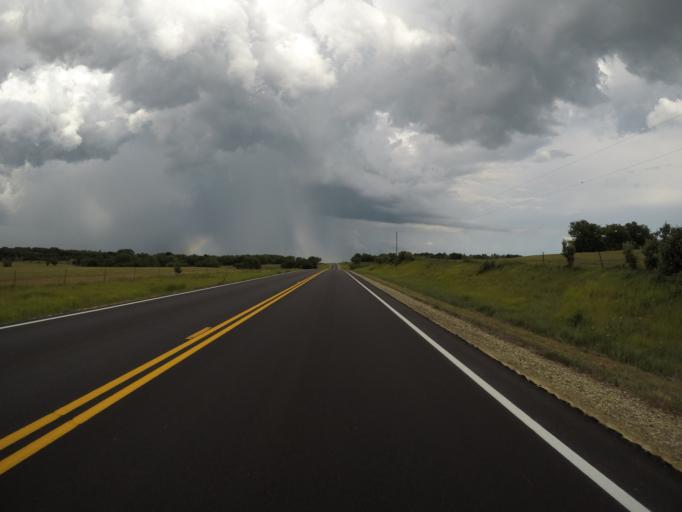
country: US
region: Kansas
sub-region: Marshall County
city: Blue Rapids
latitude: 39.4367
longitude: -96.8232
